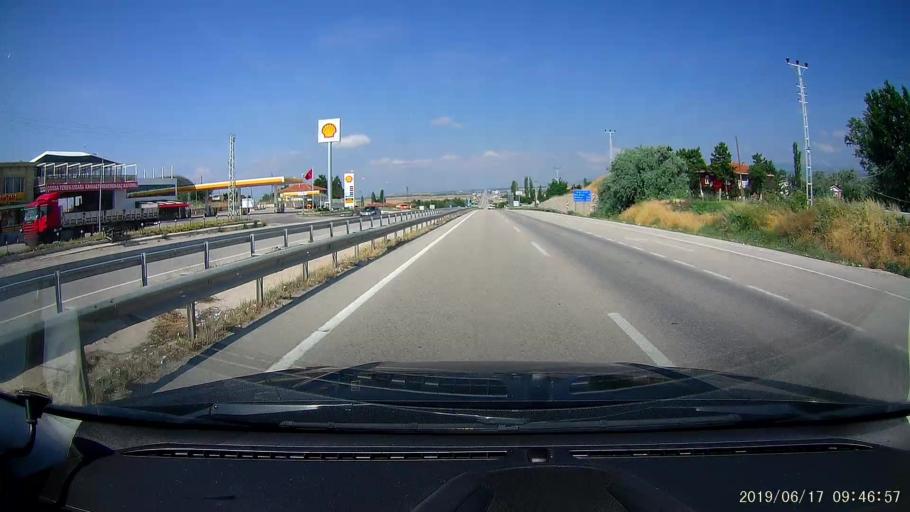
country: TR
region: Amasya
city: Suluova
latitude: 40.8775
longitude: 35.5905
